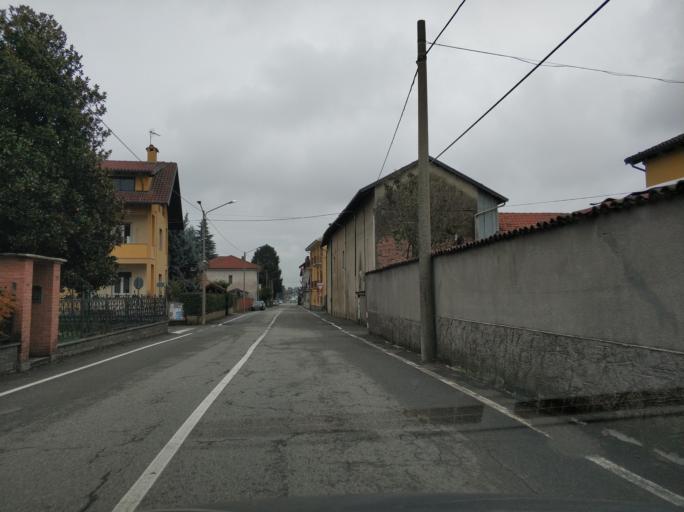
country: IT
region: Piedmont
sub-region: Provincia di Torino
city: Villanova Canavese
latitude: 45.2429
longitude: 7.5495
